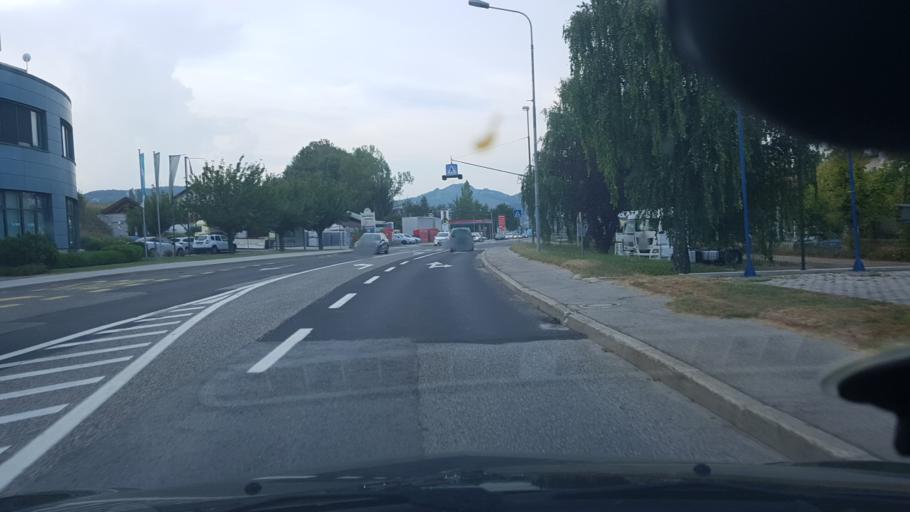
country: SI
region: Krsko
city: Leskovec pri Krskem
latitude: 45.9394
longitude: 15.4845
